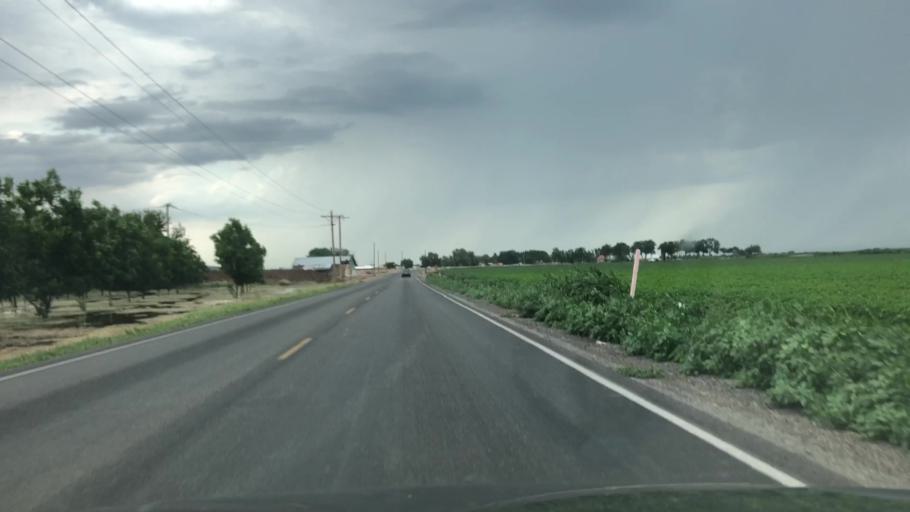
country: US
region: New Mexico
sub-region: Dona Ana County
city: Anthony
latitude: 32.0218
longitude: -106.6702
